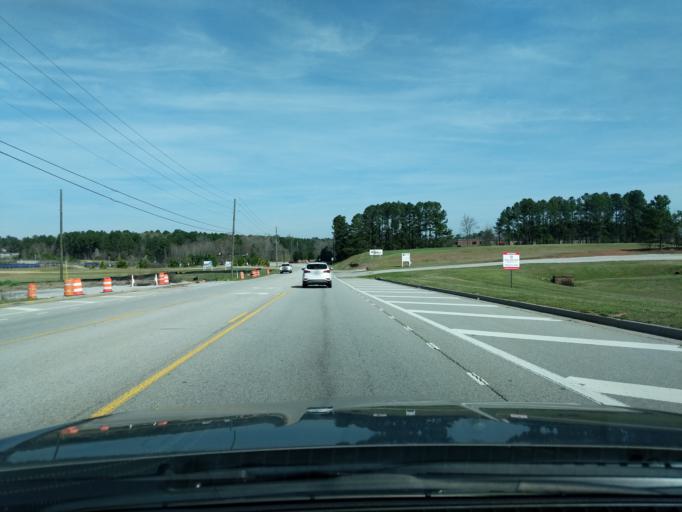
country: US
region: Georgia
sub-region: Columbia County
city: Evans
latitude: 33.5432
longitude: -82.1251
